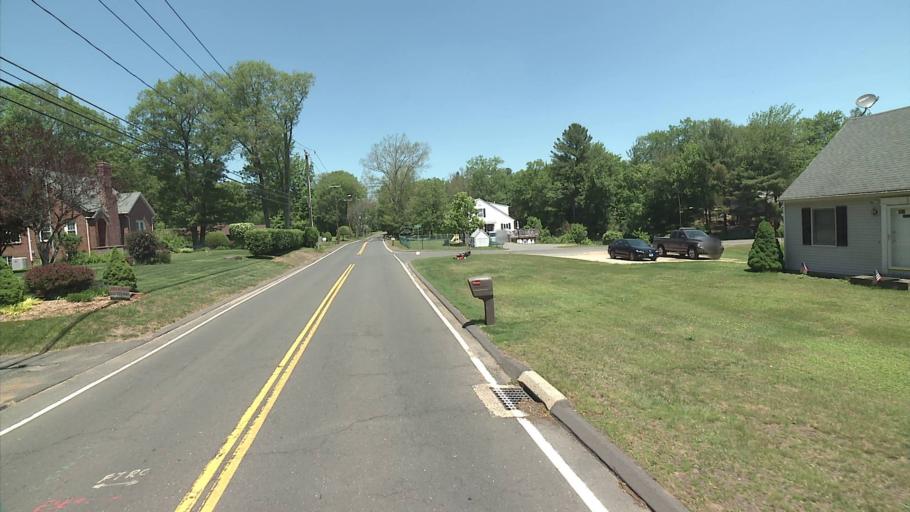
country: US
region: Connecticut
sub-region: Tolland County
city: Stafford Springs
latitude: 41.9606
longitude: -72.2964
